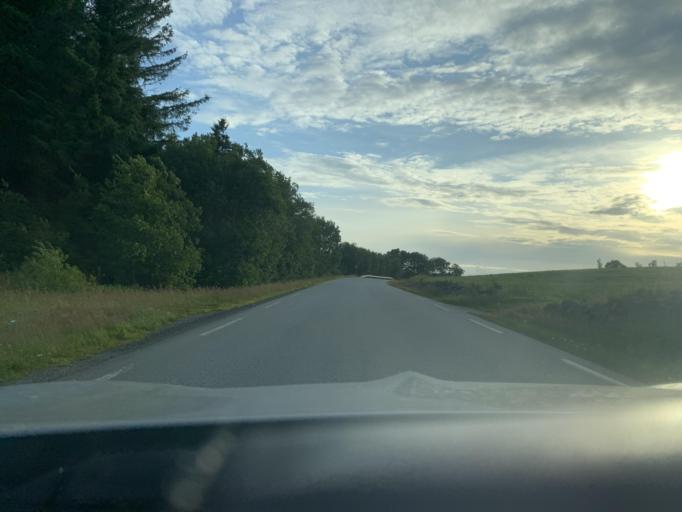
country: NO
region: Rogaland
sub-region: Ha
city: Naerbo
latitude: 58.6850
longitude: 5.7383
